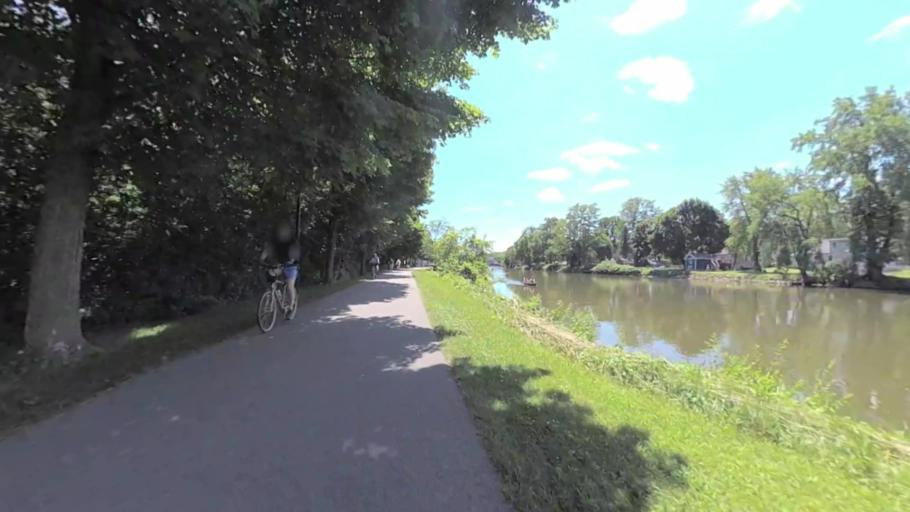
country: US
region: New York
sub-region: Monroe County
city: Fairport
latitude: 43.1043
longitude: -77.4457
